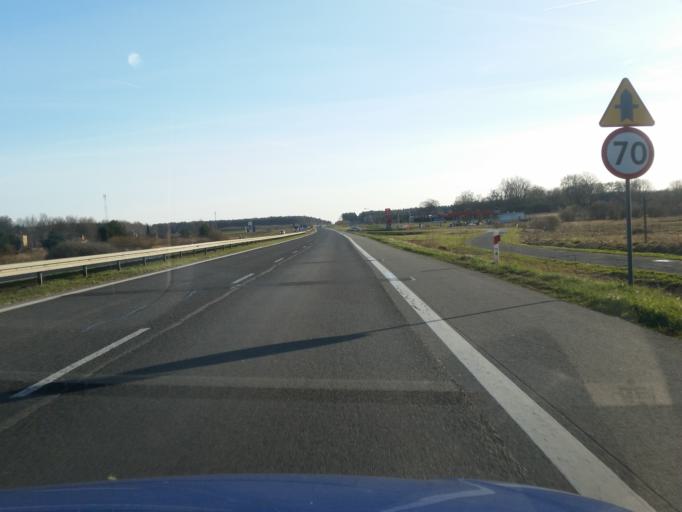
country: PL
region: Silesian Voivodeship
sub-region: Powiat czestochowski
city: Borowno
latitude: 50.9991
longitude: 19.2925
